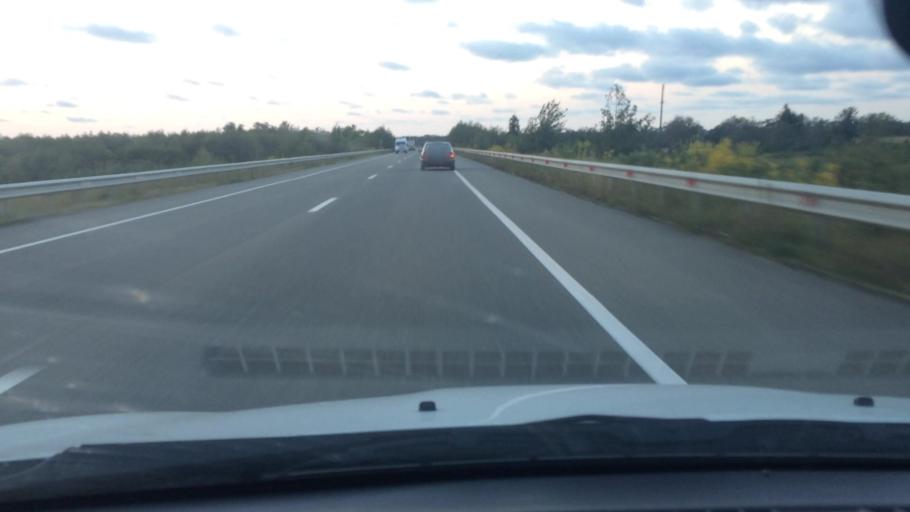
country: GE
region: Ajaria
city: Ochkhamuri
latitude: 41.9069
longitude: 41.7869
